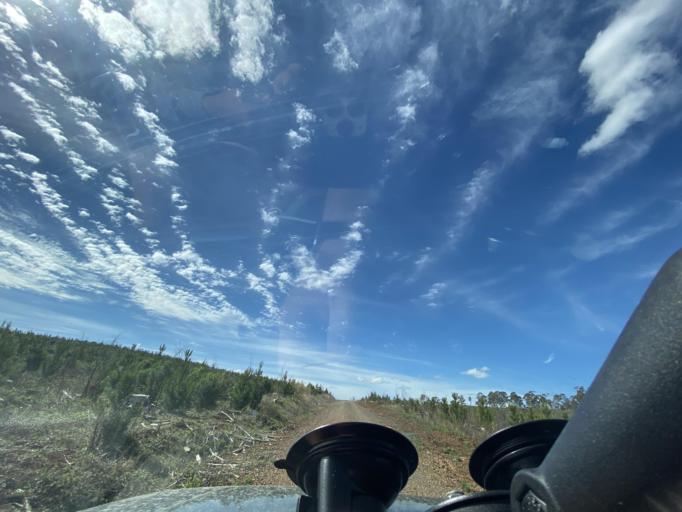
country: AU
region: Victoria
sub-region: Mansfield
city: Mansfield
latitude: -36.8297
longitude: 146.1020
